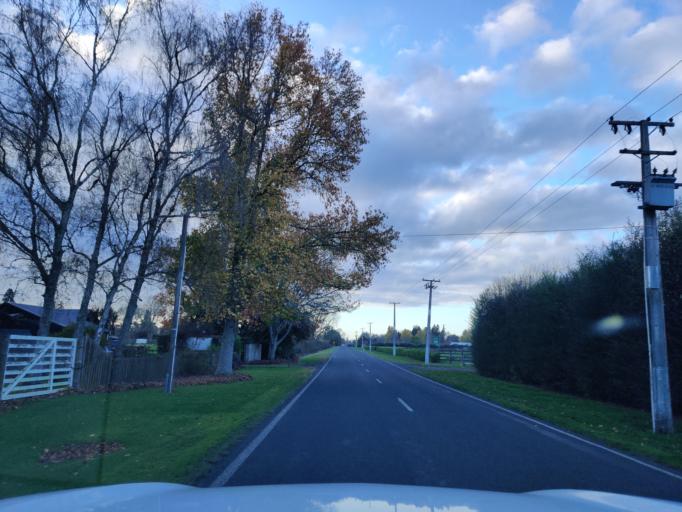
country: NZ
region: Waikato
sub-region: Waipa District
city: Cambridge
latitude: -37.8577
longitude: 175.4390
